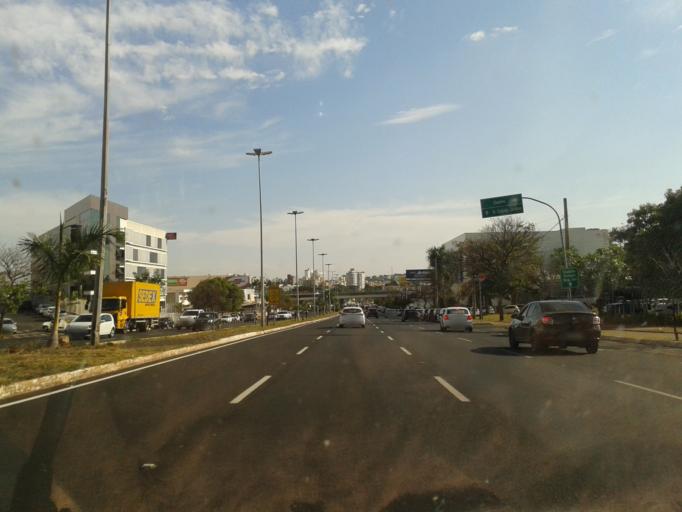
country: BR
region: Minas Gerais
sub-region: Uberlandia
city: Uberlandia
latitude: -18.9282
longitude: -48.2755
